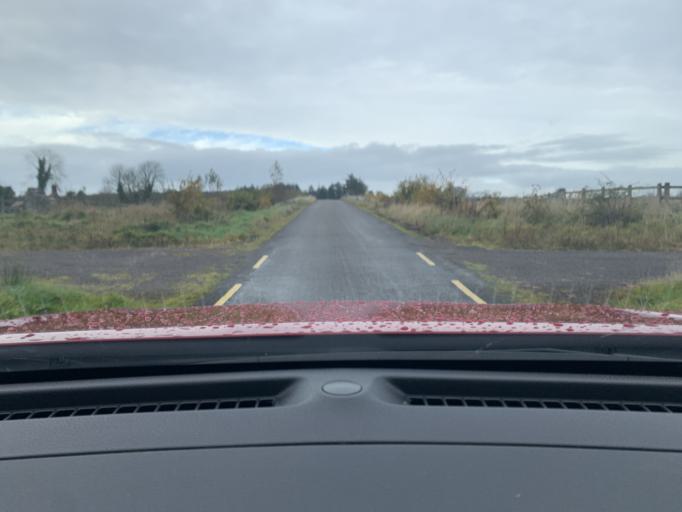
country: IE
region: Connaught
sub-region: Roscommon
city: Ballaghaderreen
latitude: 53.9141
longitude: -8.5660
